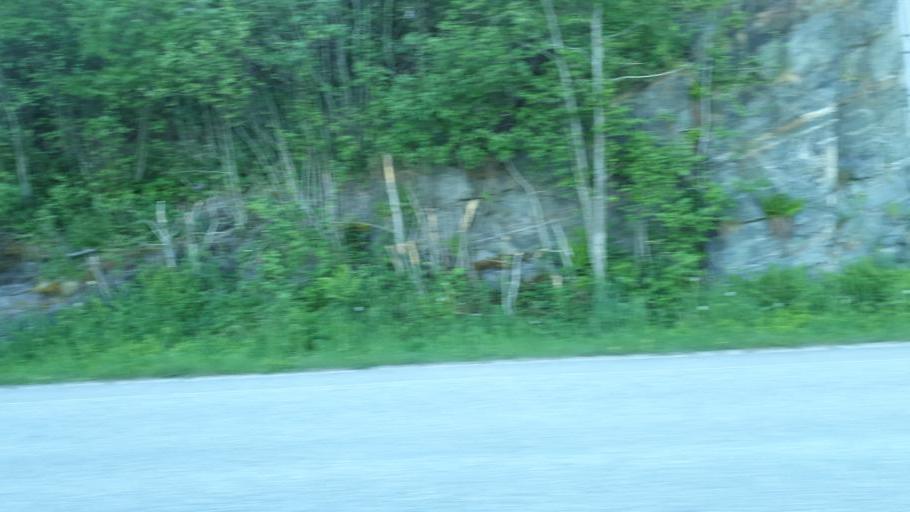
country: NO
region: Sor-Trondelag
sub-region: Rissa
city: Rissa
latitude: 63.5072
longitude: 10.1314
